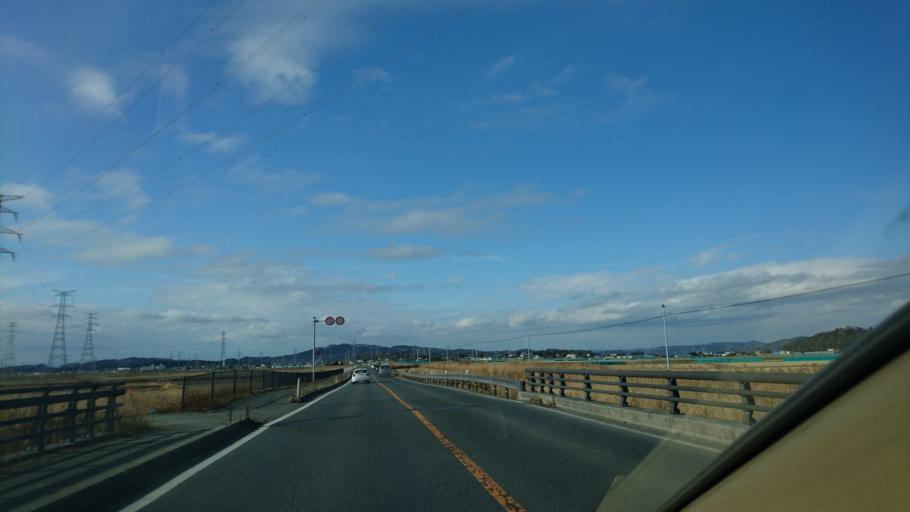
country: JP
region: Miyagi
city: Yamoto
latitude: 38.4682
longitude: 141.2373
